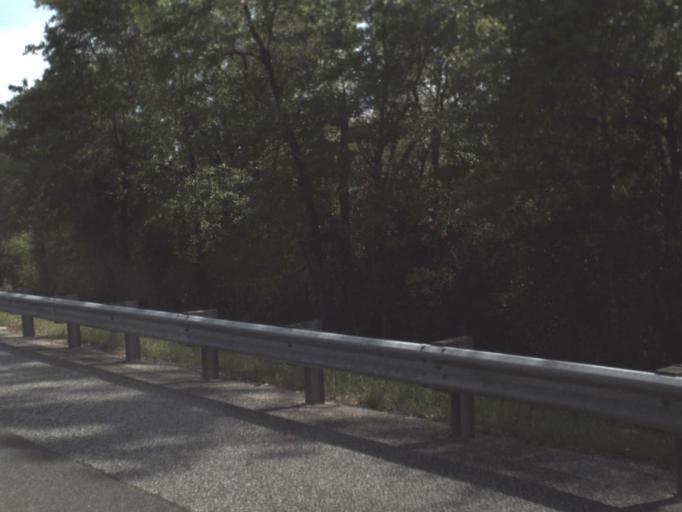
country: US
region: Florida
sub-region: Santa Rosa County
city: East Milton
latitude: 30.5824
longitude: -86.9294
